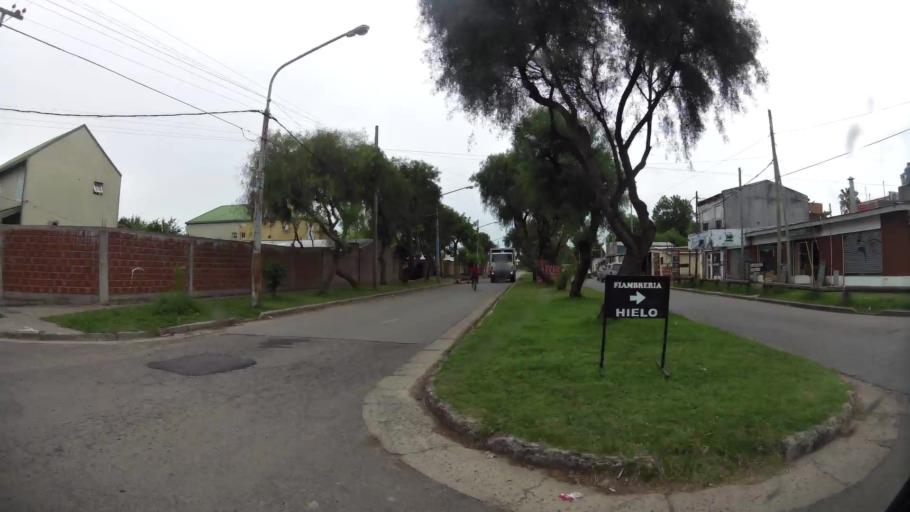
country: AR
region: Buenos Aires
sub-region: Partido de Campana
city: Campana
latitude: -34.1978
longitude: -58.9431
